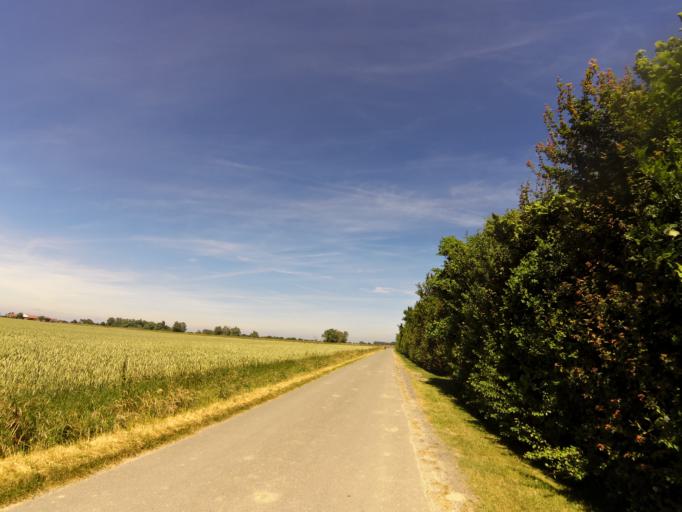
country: NL
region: Zeeland
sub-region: Gemeente Sluis
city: Sluis
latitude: 51.3269
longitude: 3.3669
